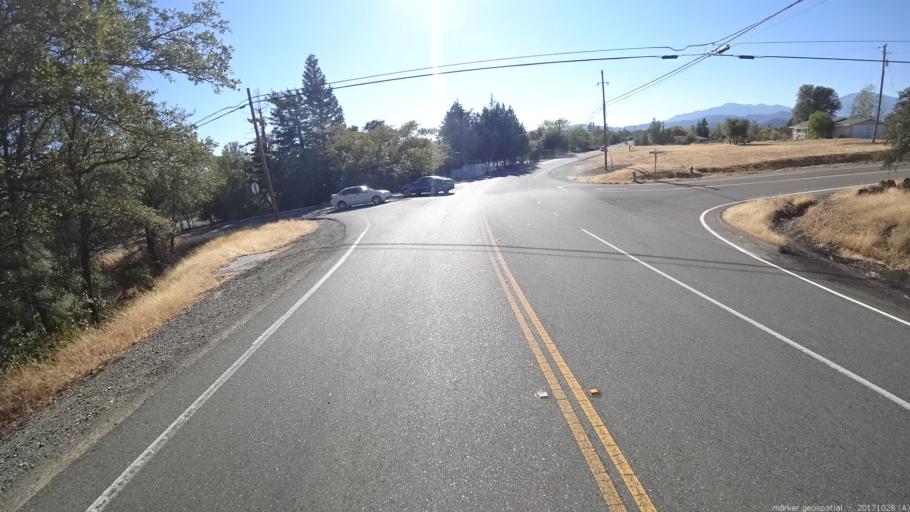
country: US
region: California
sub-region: Shasta County
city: Redding
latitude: 40.6168
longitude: -122.4281
